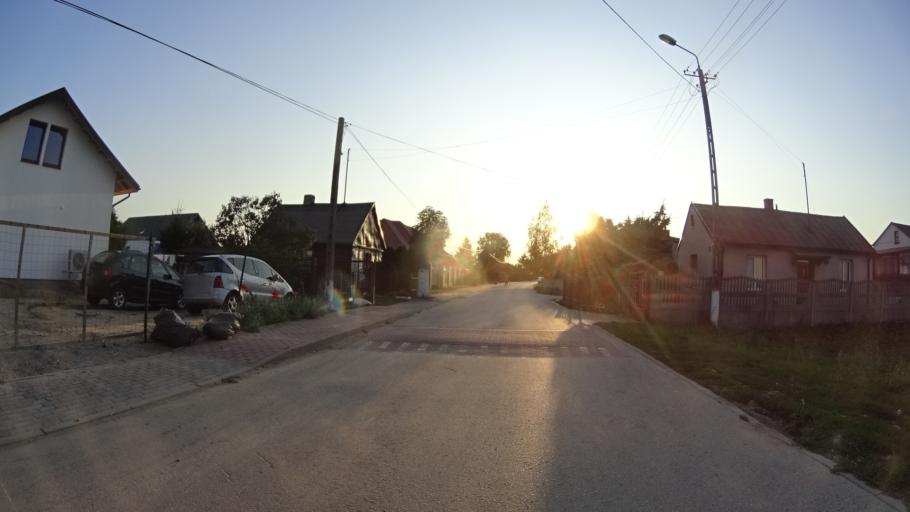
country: PL
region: Masovian Voivodeship
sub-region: Powiat warszawski zachodni
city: Ozarow Mazowiecki
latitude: 52.2408
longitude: 20.7650
